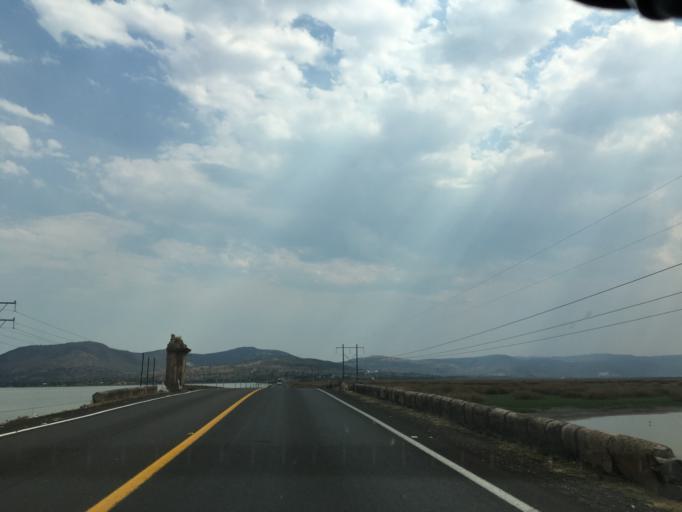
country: MX
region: Michoacan
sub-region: Cuitzeo
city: San Juan Benito Juarez (San Juan Tararameo)
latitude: 19.9424
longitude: -101.1379
